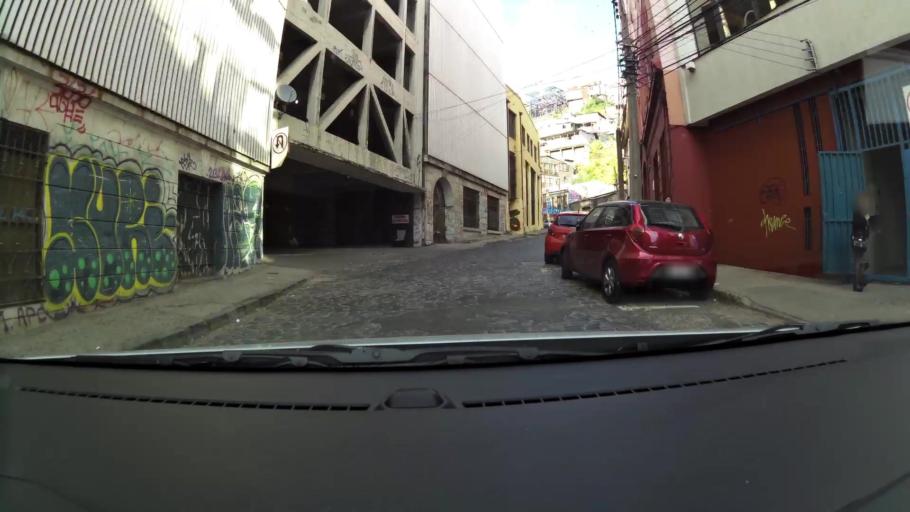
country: CL
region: Valparaiso
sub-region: Provincia de Valparaiso
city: Valparaiso
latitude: -33.0398
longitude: -71.6307
